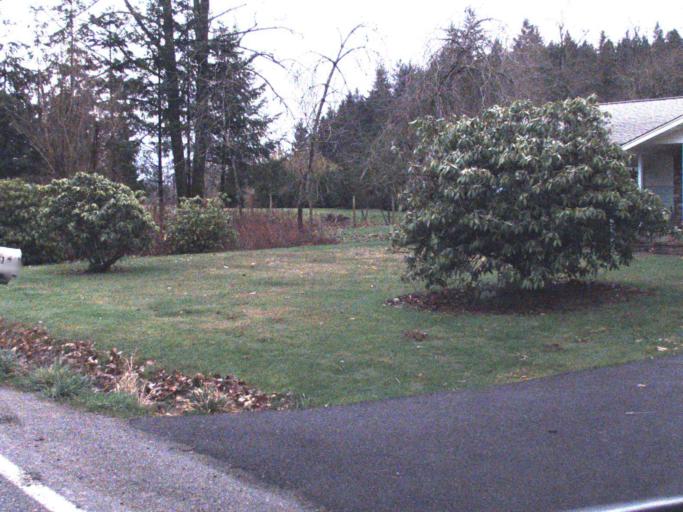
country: US
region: Washington
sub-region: Snohomish County
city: Smokey Point
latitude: 48.1520
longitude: -122.2252
